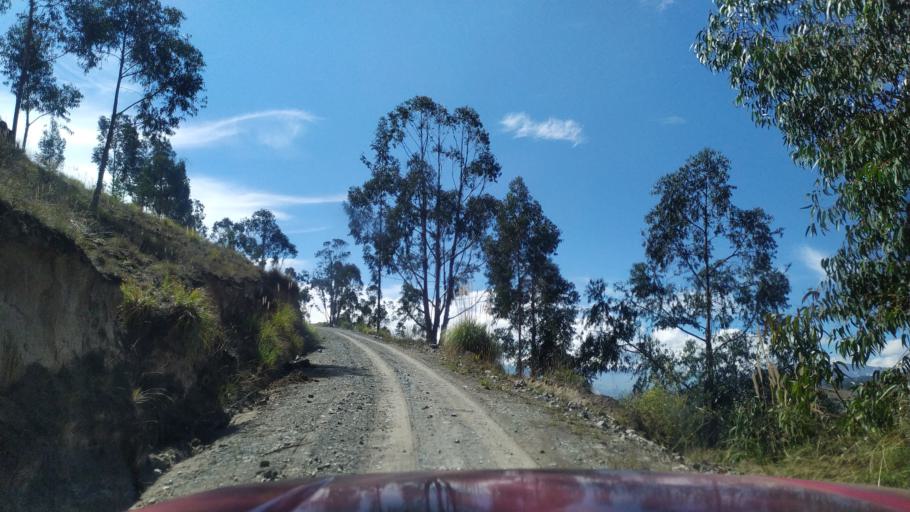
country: EC
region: Chimborazo
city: Riobamba
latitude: -1.6782
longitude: -78.6949
